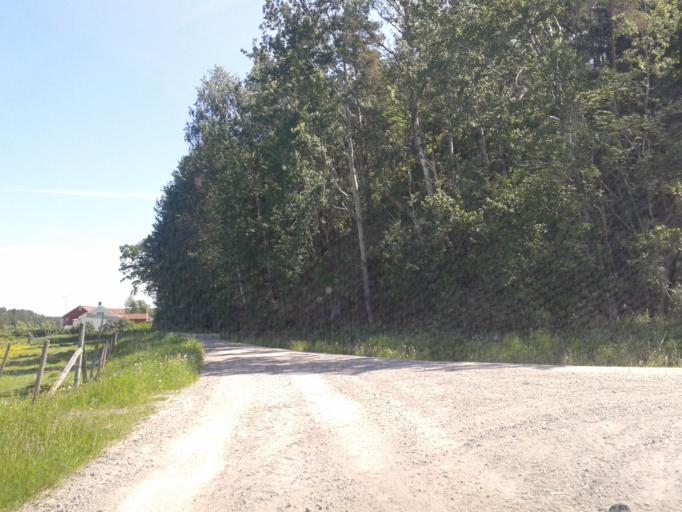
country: SE
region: Vaestra Goetaland
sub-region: Stromstads Kommun
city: Stroemstad
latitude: 58.8624
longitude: 11.2198
